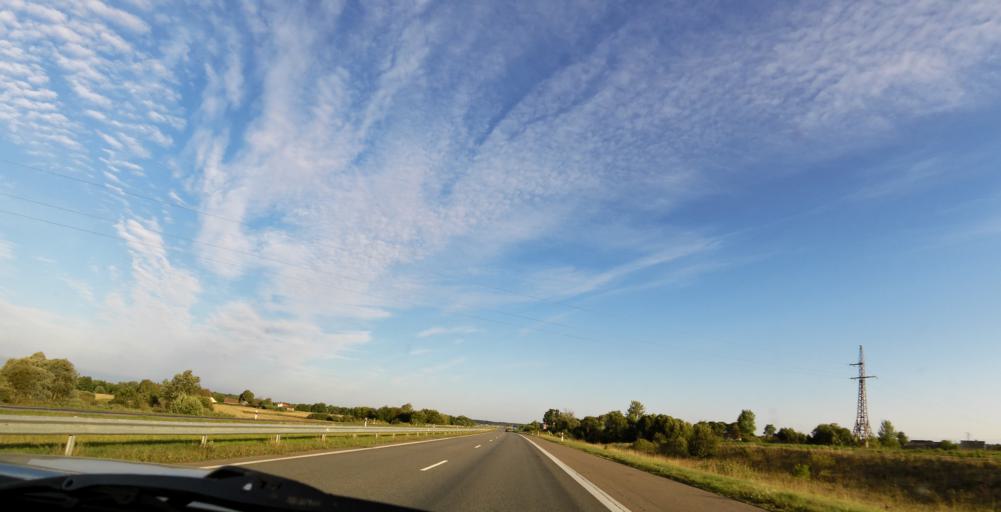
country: LT
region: Vilnius County
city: Ukmerge
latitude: 55.3080
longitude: 24.7897
